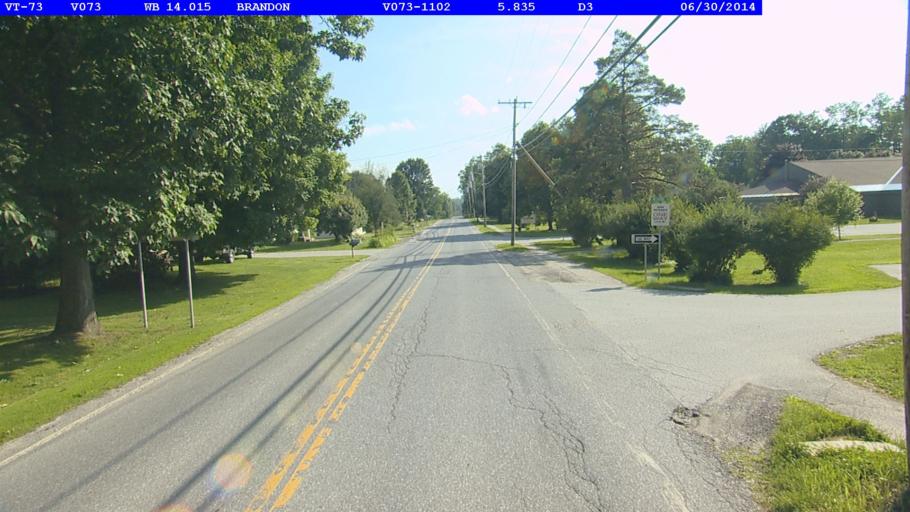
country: US
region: Vermont
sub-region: Rutland County
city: Brandon
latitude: 43.8266
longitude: -73.0537
